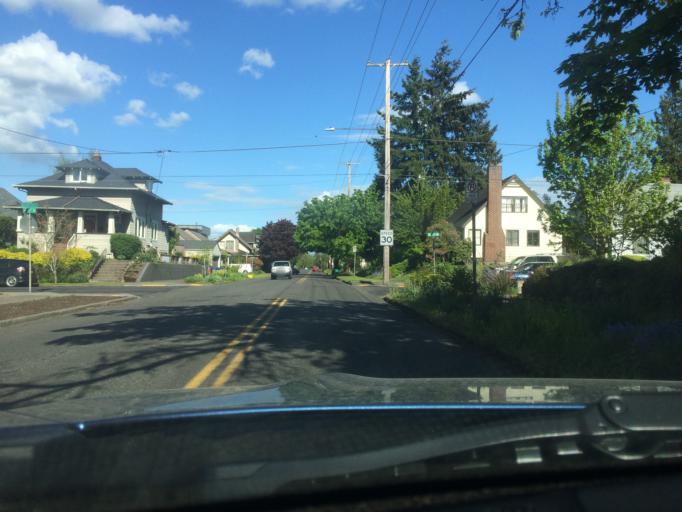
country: US
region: Oregon
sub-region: Multnomah County
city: Portland
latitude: 45.5554
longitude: -122.6404
